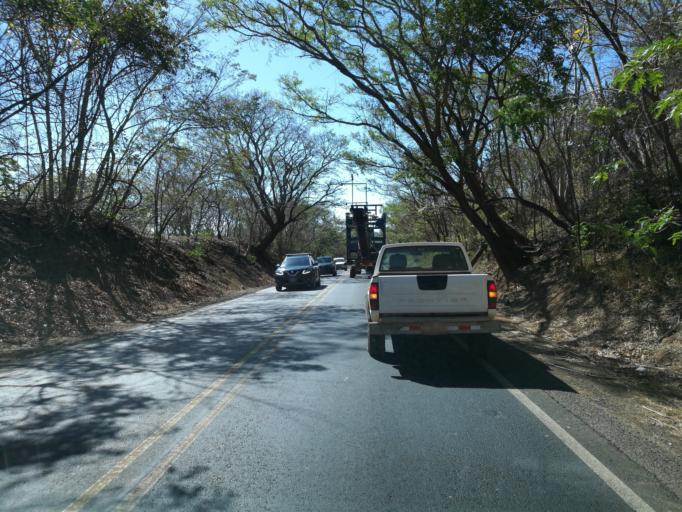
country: CR
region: Puntarenas
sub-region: Canton Central de Puntarenas
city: Puntarenas
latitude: 10.0949
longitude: -84.8562
